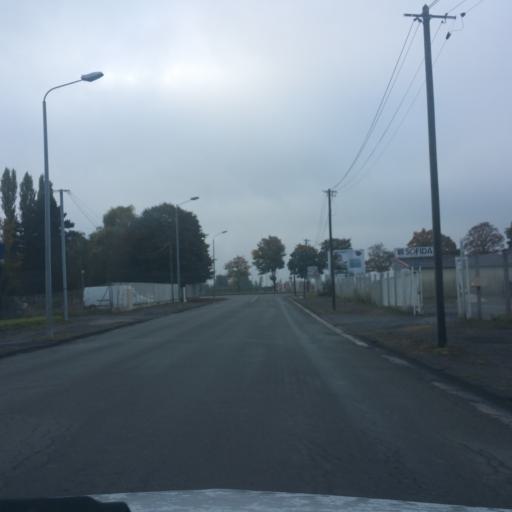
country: FR
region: Picardie
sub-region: Departement de l'Aisne
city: Laon
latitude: 49.5778
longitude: 3.6458
